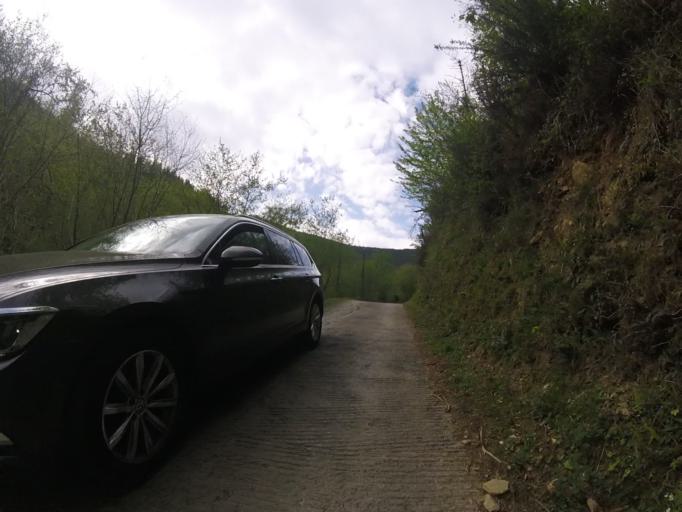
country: ES
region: Basque Country
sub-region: Provincia de Guipuzcoa
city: Errezil
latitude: 43.2029
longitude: -2.1848
